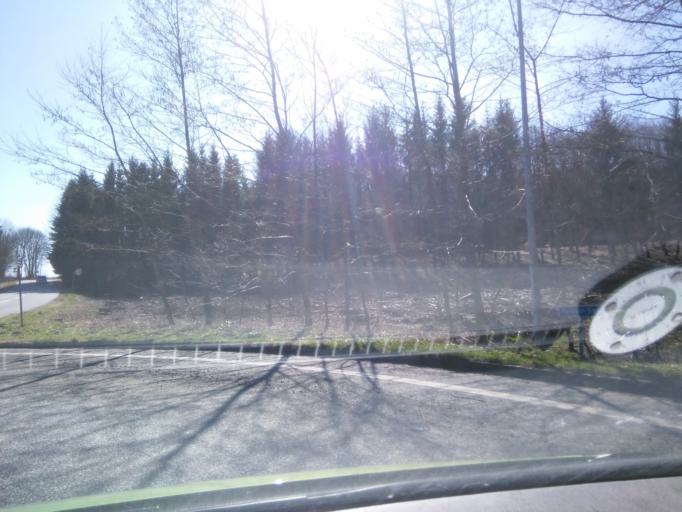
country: DK
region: Central Jutland
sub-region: Favrskov Kommune
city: Hinnerup
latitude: 56.2612
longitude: 10.0574
